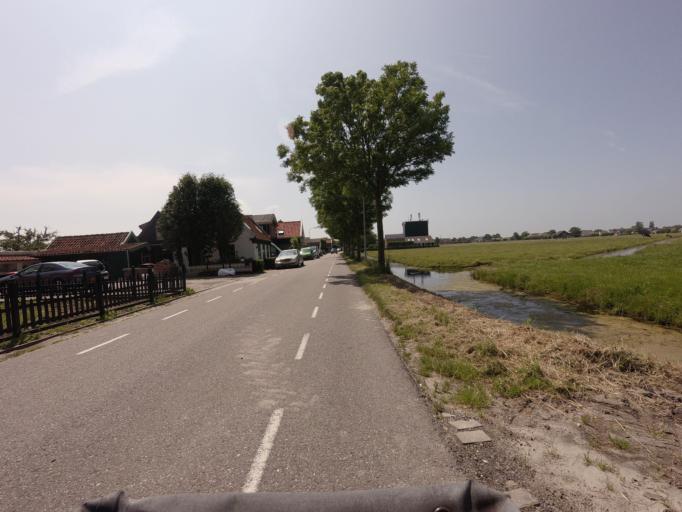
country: NL
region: North Holland
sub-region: Gemeente Opmeer
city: Opmeer
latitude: 52.6543
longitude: 4.9472
